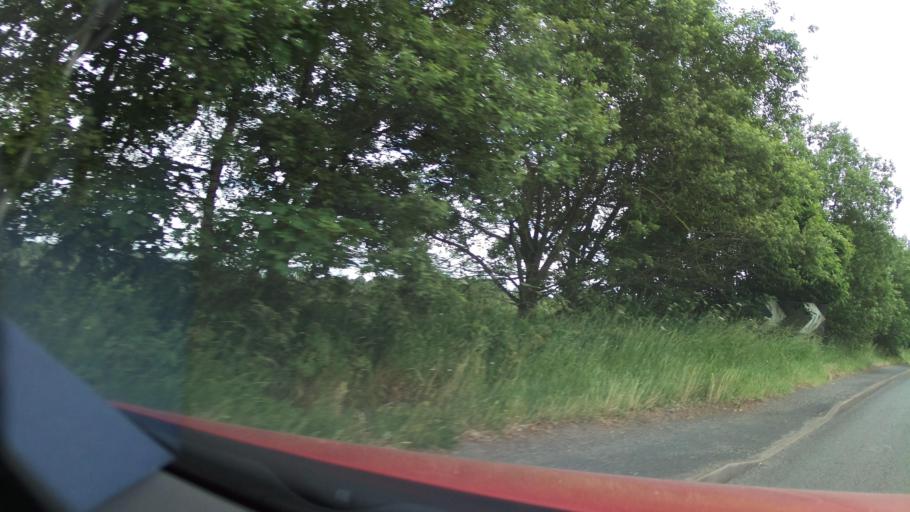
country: GB
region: England
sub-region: Dudley
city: Kingswinford
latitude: 52.4682
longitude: -2.1976
